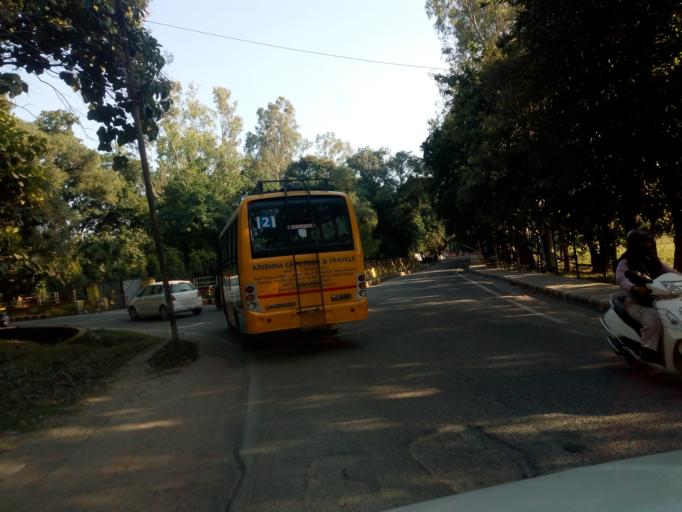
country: IN
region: Uttarakhand
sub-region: Dehradun
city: Dehradun
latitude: 30.3514
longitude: 78.0335
